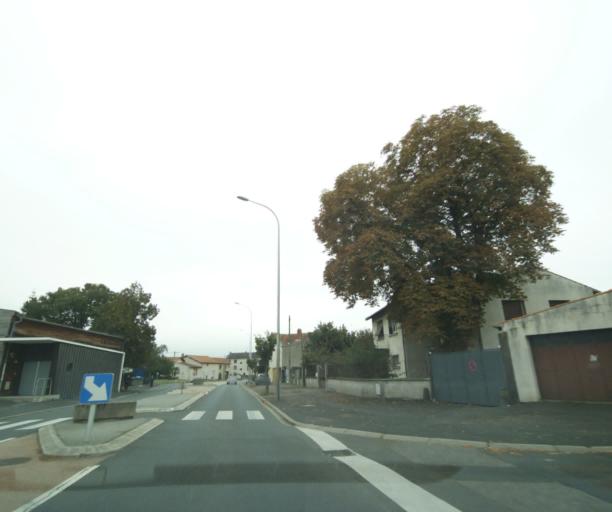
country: FR
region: Auvergne
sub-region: Departement du Puy-de-Dome
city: Gerzat
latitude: 45.8243
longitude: 3.1418
